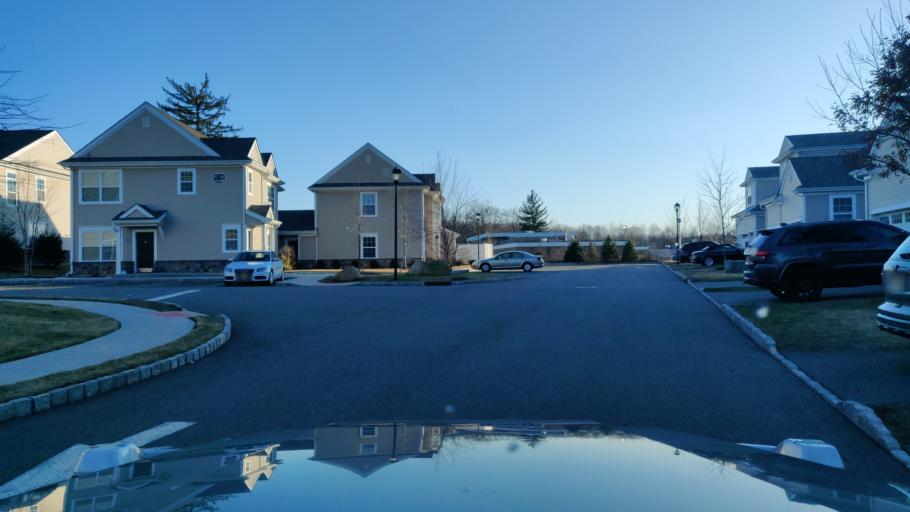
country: US
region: New Jersey
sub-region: Essex County
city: Westville
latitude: 40.8568
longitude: -74.3092
